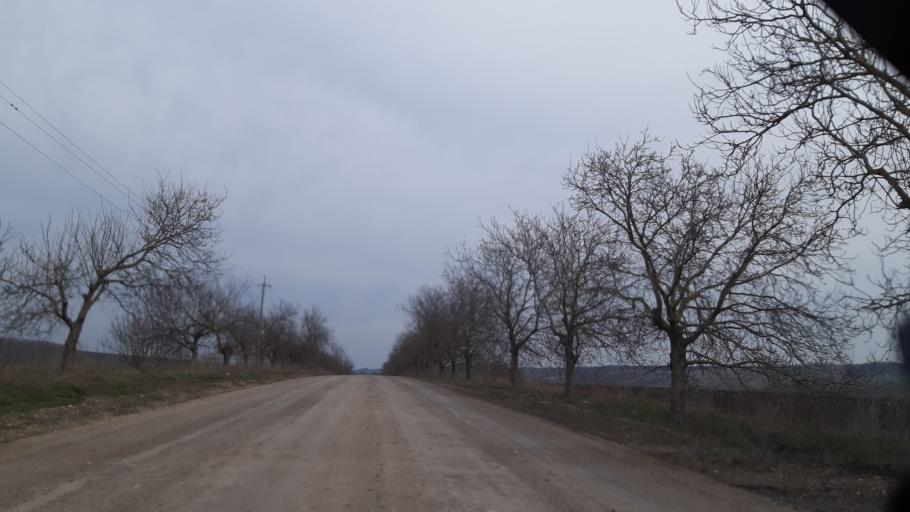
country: MD
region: Soldanesti
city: Soldanesti
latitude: 47.7010
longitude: 28.7221
